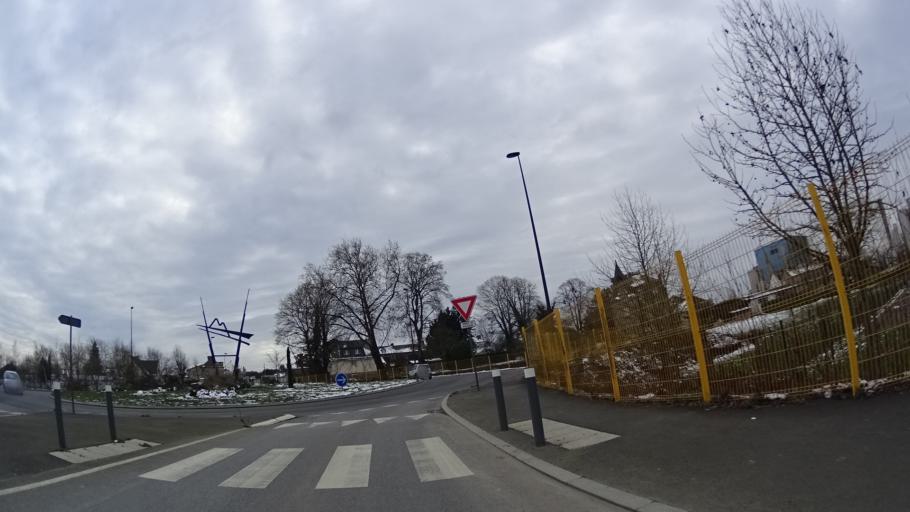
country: FR
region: Brittany
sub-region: Departement d'Ille-et-Vilaine
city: Montauban-de-Bretagne
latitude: 48.1918
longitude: -2.0510
